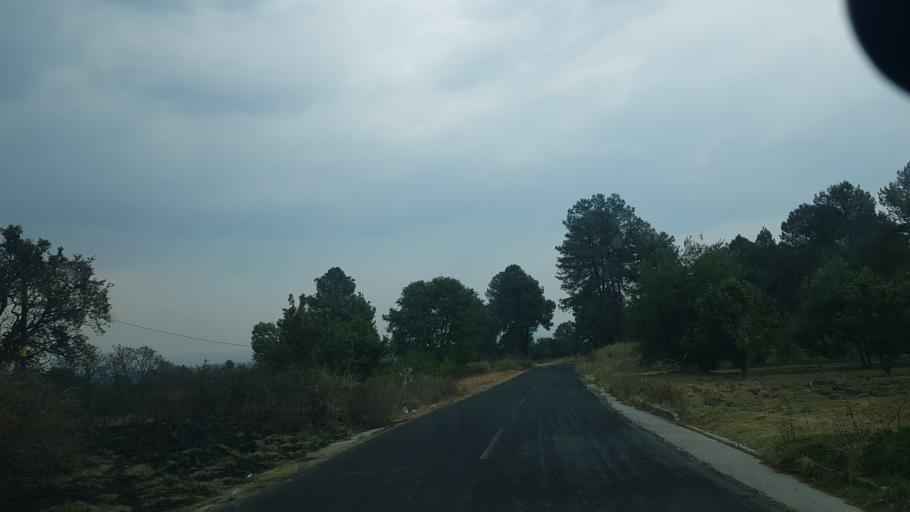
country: MX
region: Puebla
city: San Lorenzo Chiautzingo
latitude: 19.1907
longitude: -98.4744
